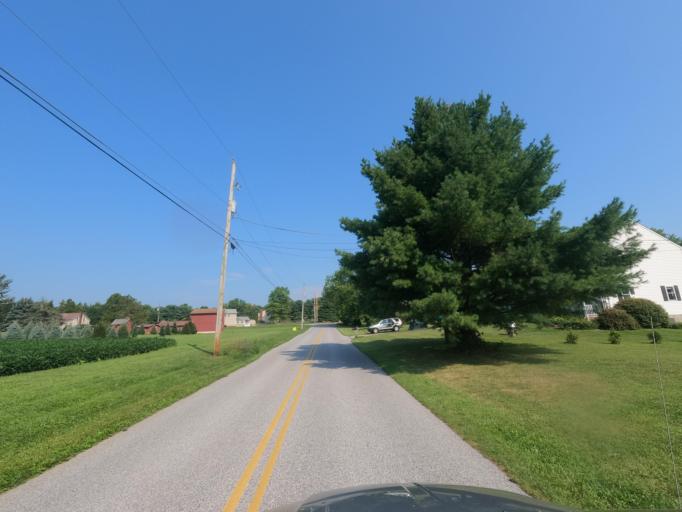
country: US
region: Pennsylvania
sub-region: York County
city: Shrewsbury
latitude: 39.7831
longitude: -76.6633
